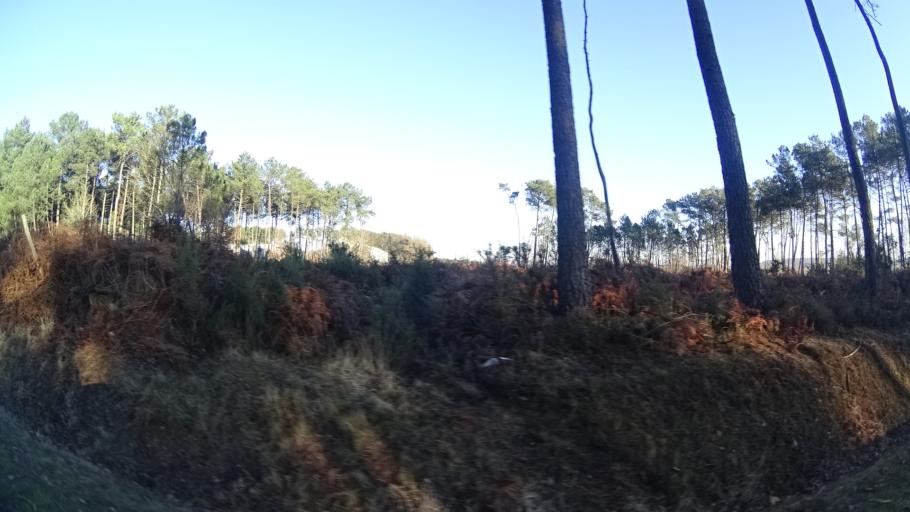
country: FR
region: Brittany
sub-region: Departement du Morbihan
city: Saint-Jacut-les-Pins
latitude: 47.6763
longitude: -2.1827
